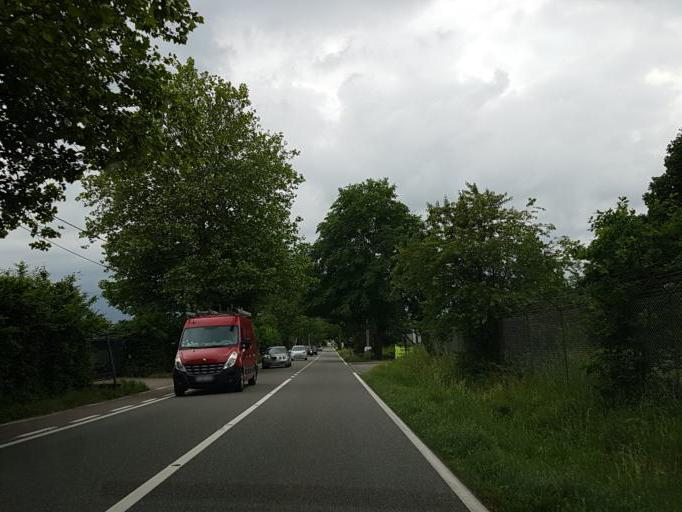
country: BE
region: Flanders
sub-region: Provincie Antwerpen
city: Nijlen
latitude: 51.1714
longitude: 4.6217
